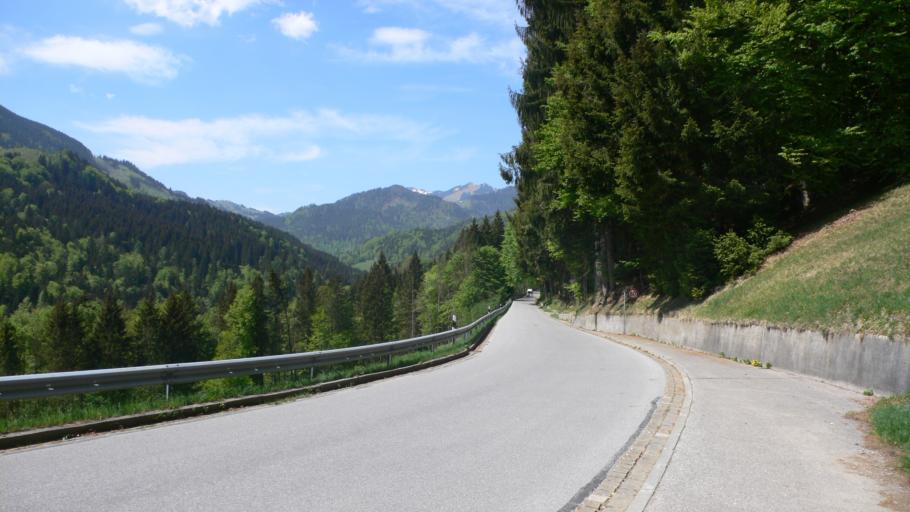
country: DE
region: Bavaria
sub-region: Upper Bavaria
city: Burg Unter-Falkenstein
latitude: 47.6722
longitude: 12.0754
